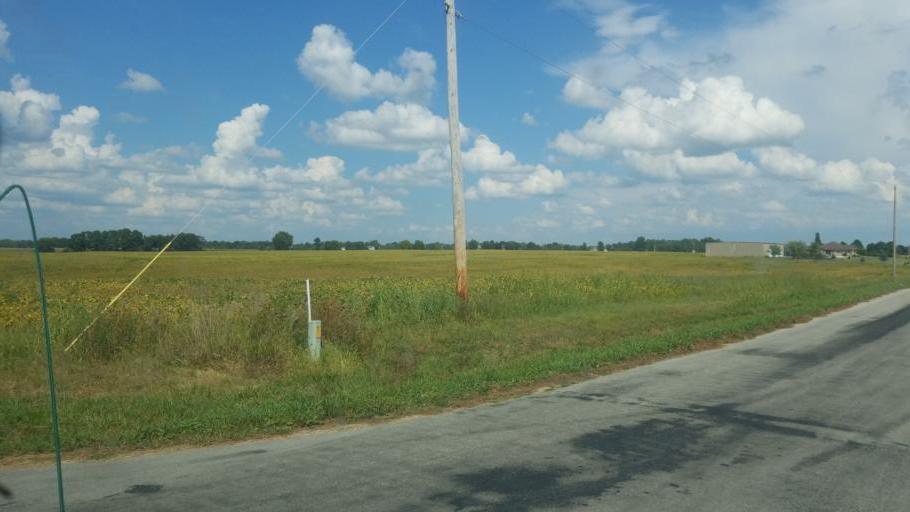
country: US
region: Ohio
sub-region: Seneca County
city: Tiffin
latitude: 40.9786
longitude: -83.1800
